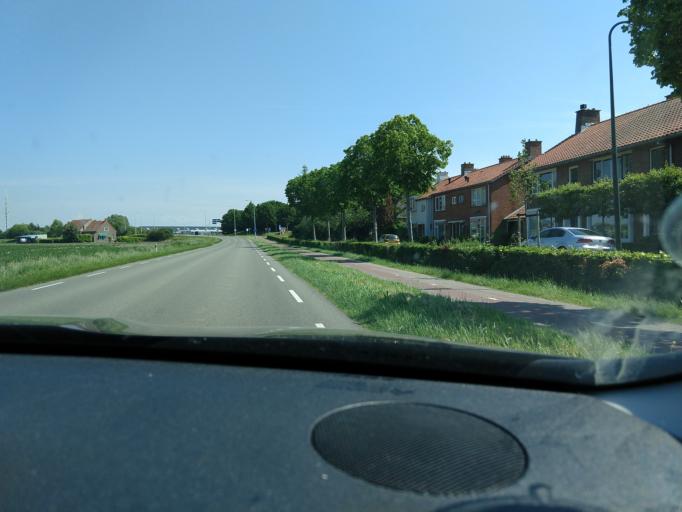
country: NL
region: Zeeland
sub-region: Gemeente Reimerswaal
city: Yerseke
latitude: 51.5499
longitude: 4.0829
